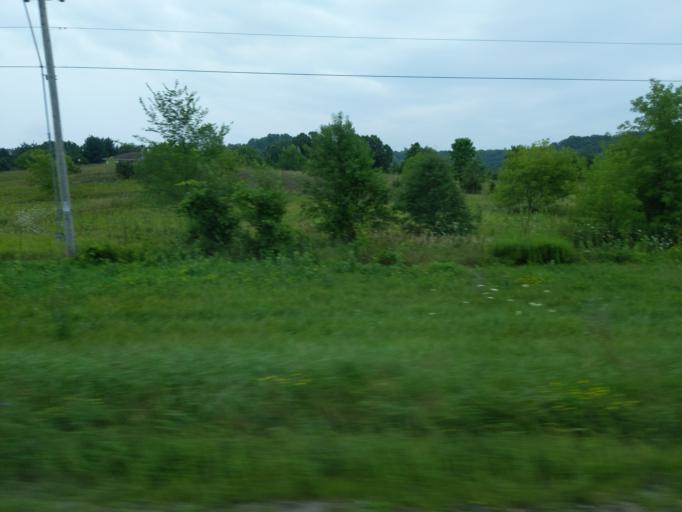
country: US
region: Wisconsin
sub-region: Dane County
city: Mazomanie
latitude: 43.1994
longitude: -89.7532
